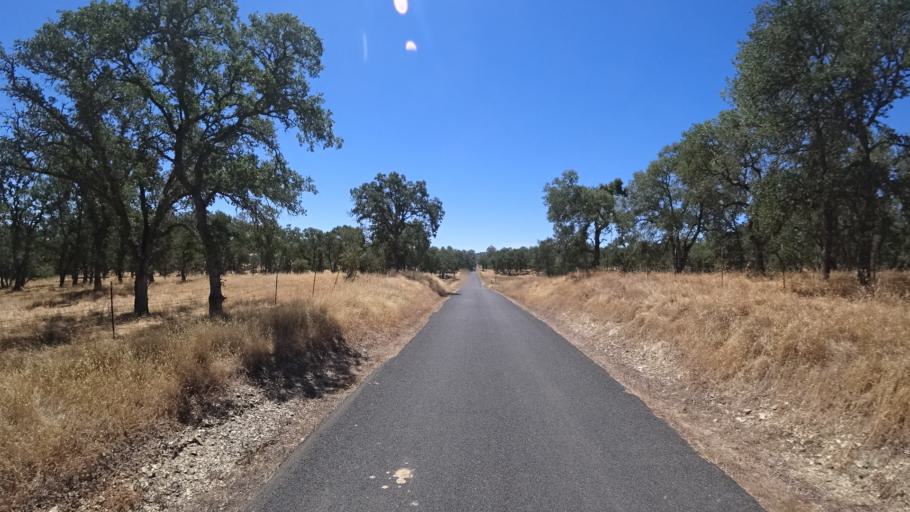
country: US
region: California
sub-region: Calaveras County
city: Copperopolis
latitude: 37.9811
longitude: -120.7017
